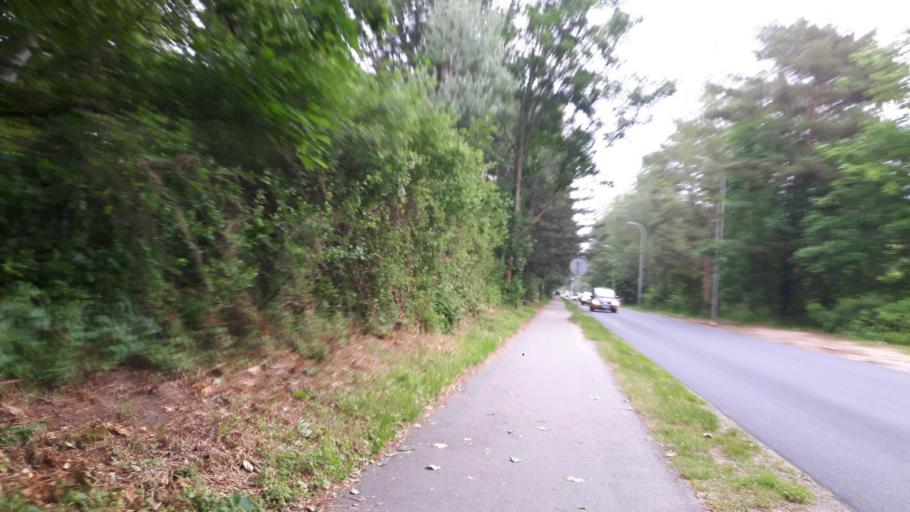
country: PL
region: West Pomeranian Voivodeship
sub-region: Powiat koszalinski
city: Mielno
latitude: 54.2716
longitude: 16.0969
